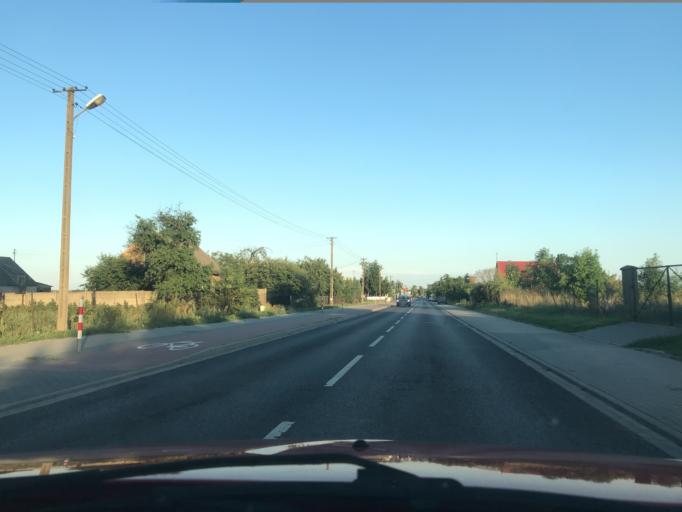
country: PL
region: Greater Poland Voivodeship
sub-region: Powiat poznanski
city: Tarnowo Podgorne
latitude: 52.4327
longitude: 16.7034
